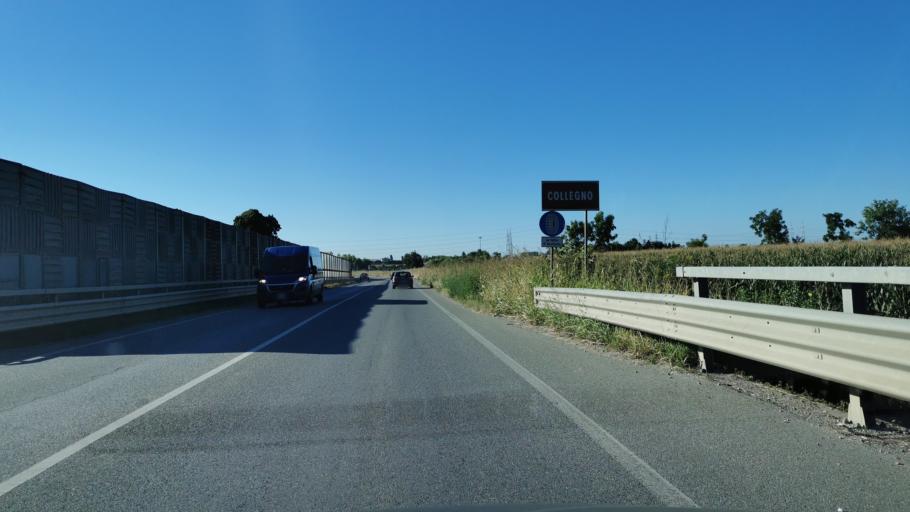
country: IT
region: Piedmont
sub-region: Provincia di Torino
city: Savonera
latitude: 45.1128
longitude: 7.5916
